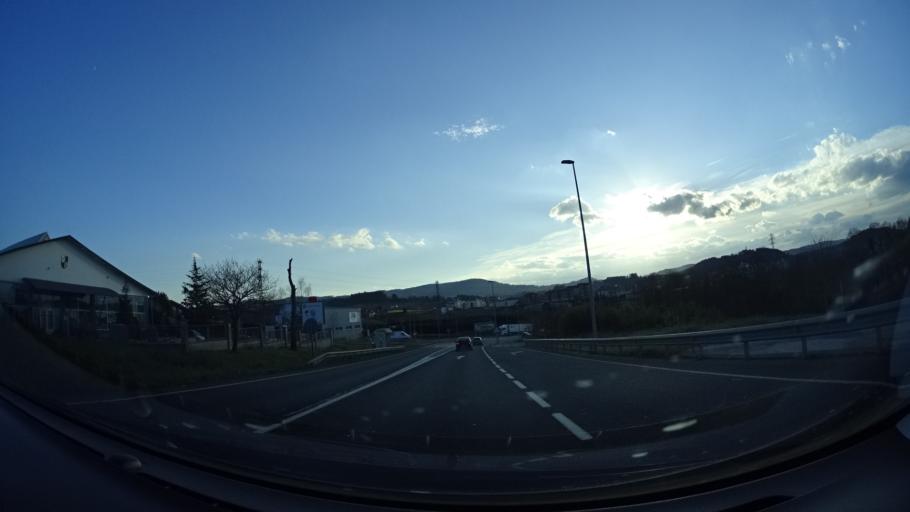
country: ES
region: Basque Country
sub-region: Bizkaia
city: Mungia
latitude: 43.3596
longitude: -2.8354
